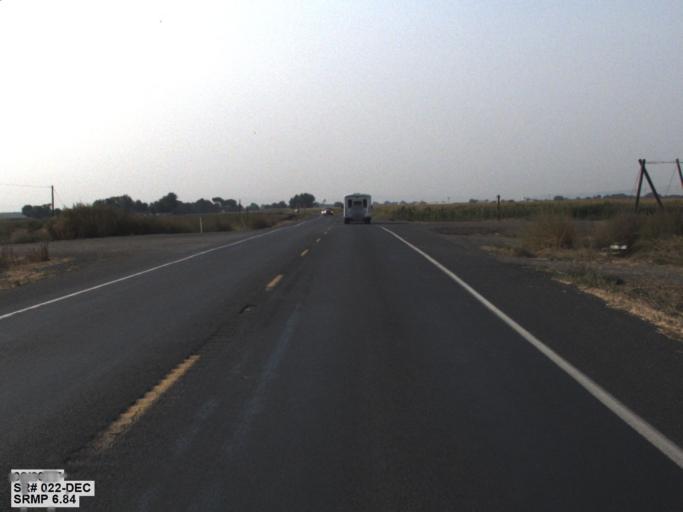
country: US
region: Washington
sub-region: Yakima County
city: Toppenish
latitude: 46.3455
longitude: -120.2725
